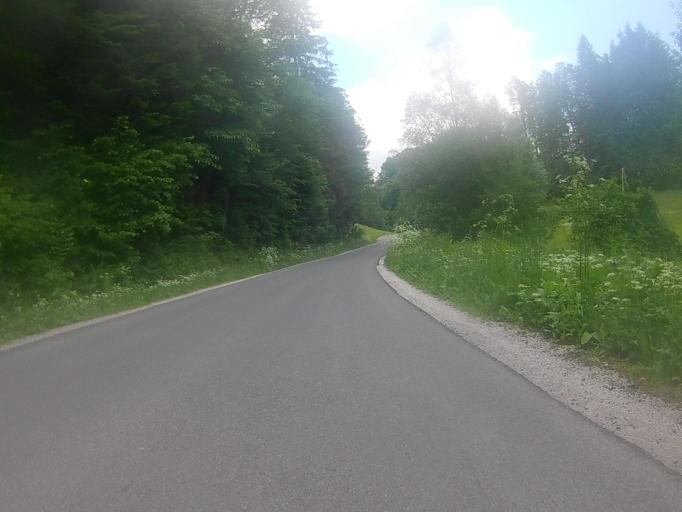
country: SI
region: Maribor
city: Bresternica
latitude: 46.6187
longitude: 15.5541
